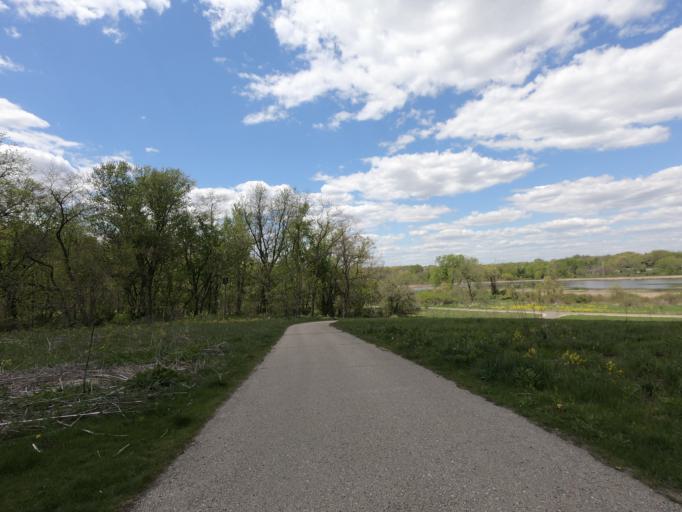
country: US
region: Wisconsin
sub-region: Dane County
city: Shorewood Hills
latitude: 43.0205
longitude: -89.4532
